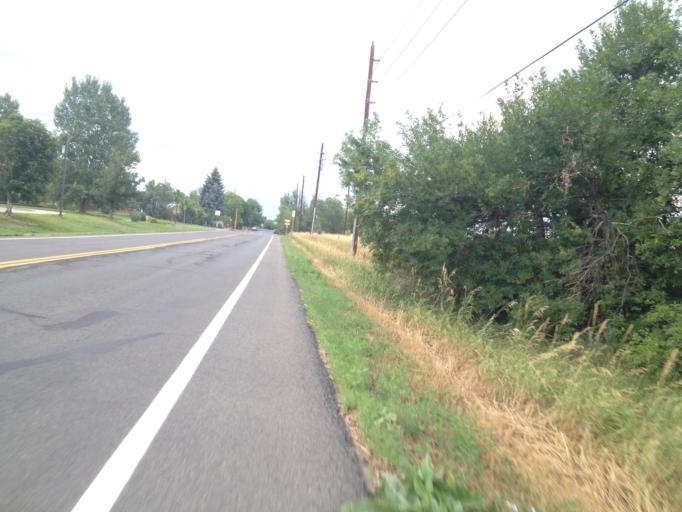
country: US
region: Colorado
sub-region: Boulder County
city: Louisville
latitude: 39.9711
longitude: -105.1292
